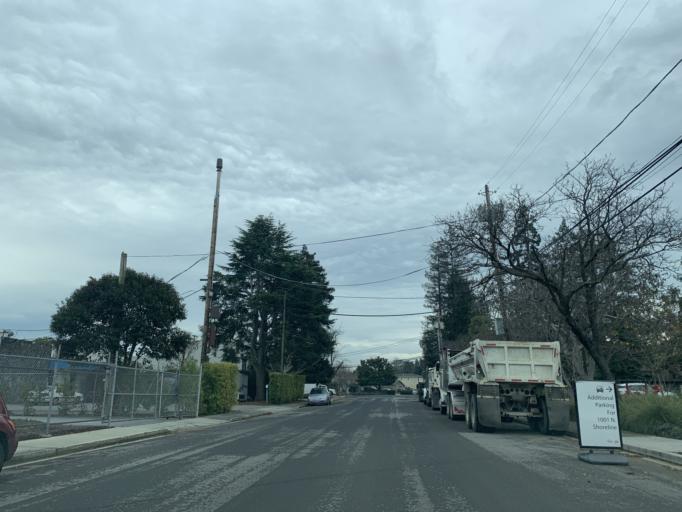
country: US
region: California
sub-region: Santa Clara County
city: Mountain View
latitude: 37.4076
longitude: -122.0755
